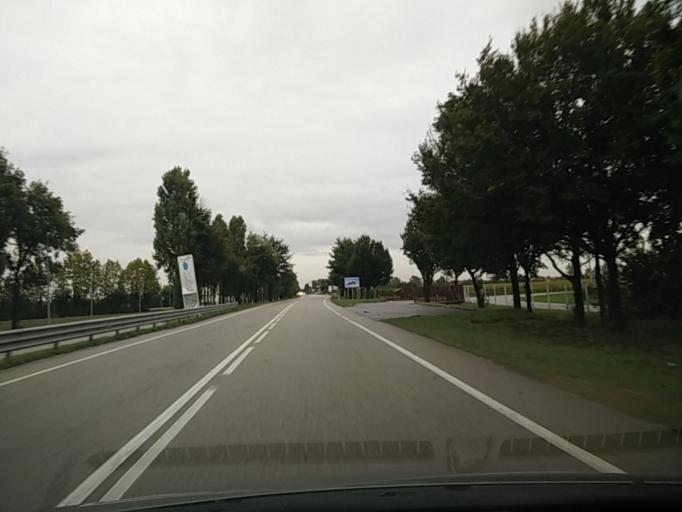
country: IT
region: Veneto
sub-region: Provincia di Treviso
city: Roncade
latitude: 45.6388
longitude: 12.3910
